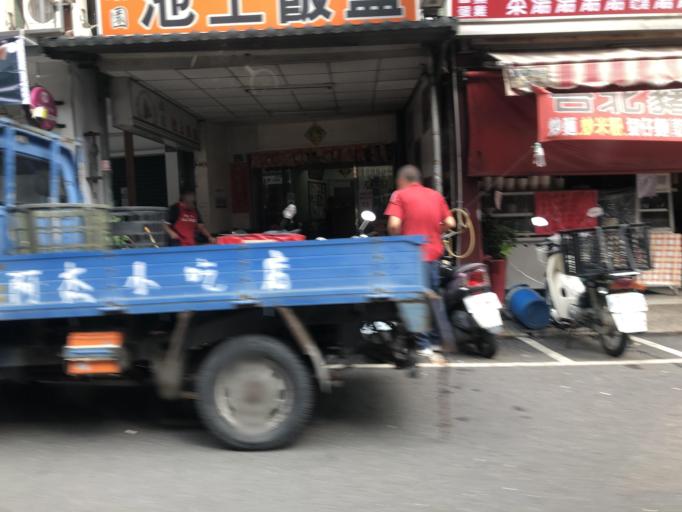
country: TW
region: Kaohsiung
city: Kaohsiung
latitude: 22.7264
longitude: 120.3052
